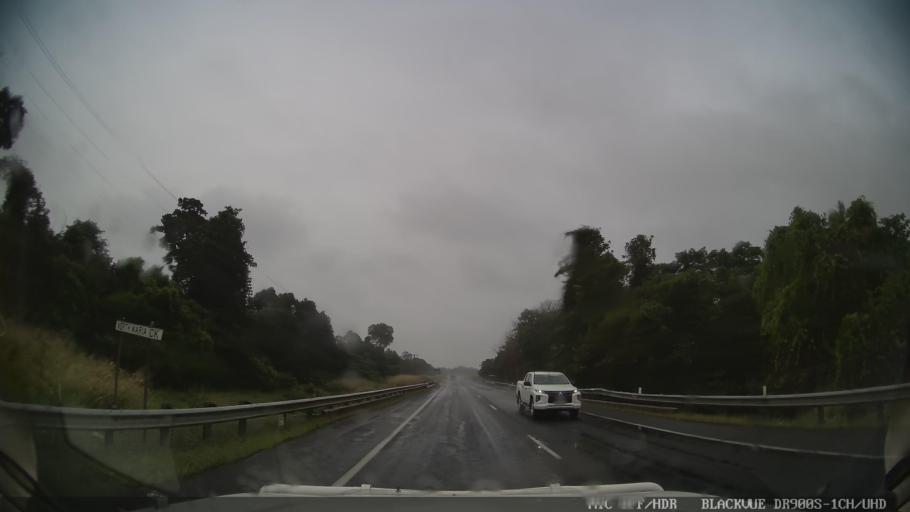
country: AU
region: Queensland
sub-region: Cassowary Coast
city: Innisfail
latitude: -17.7546
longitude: 146.0278
